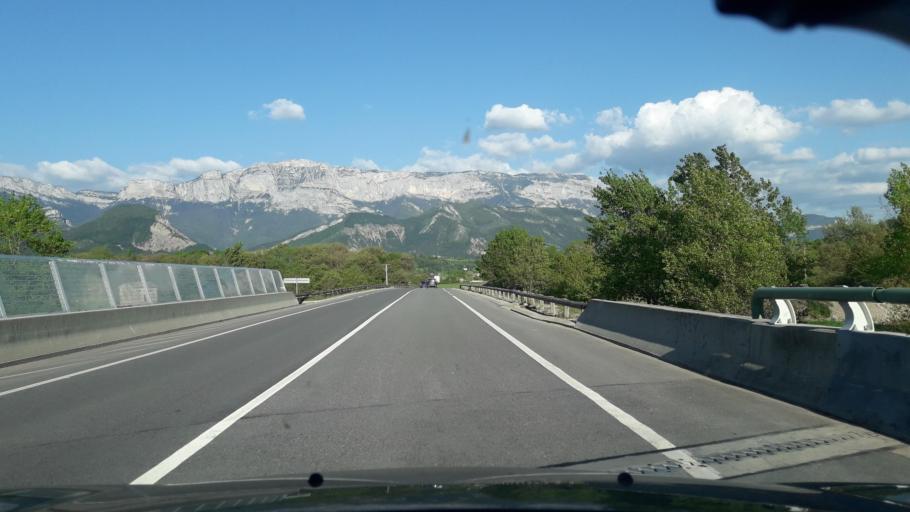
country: FR
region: Rhone-Alpes
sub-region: Departement de la Drome
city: Die
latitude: 44.7649
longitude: 5.3384
